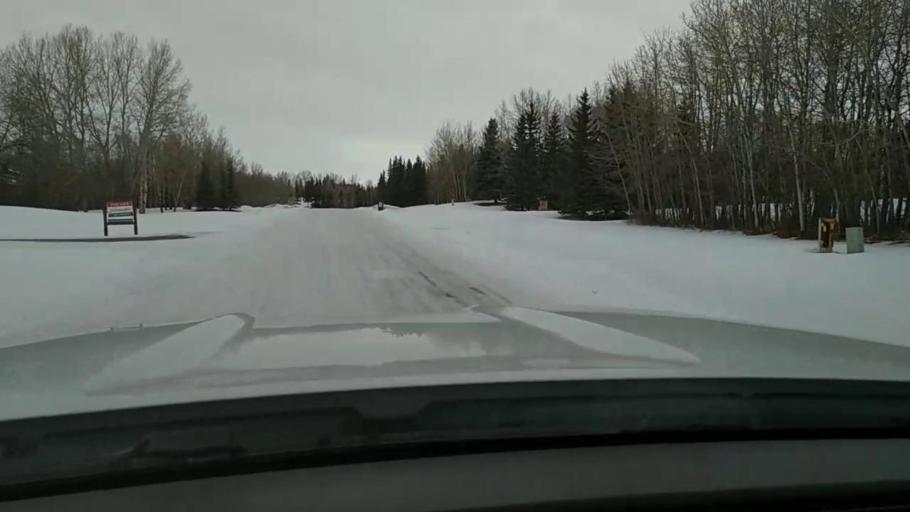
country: CA
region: Alberta
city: Calgary
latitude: 51.1564
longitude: -114.2555
